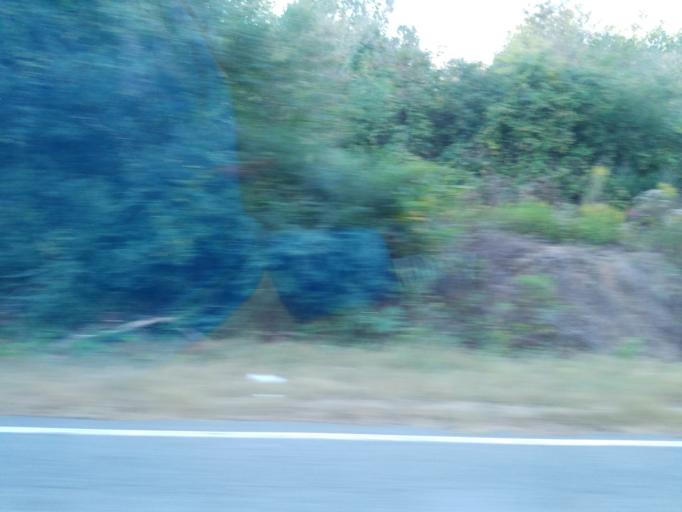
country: US
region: Georgia
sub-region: Bartow County
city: Adairsville
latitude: 34.2966
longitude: -84.9407
